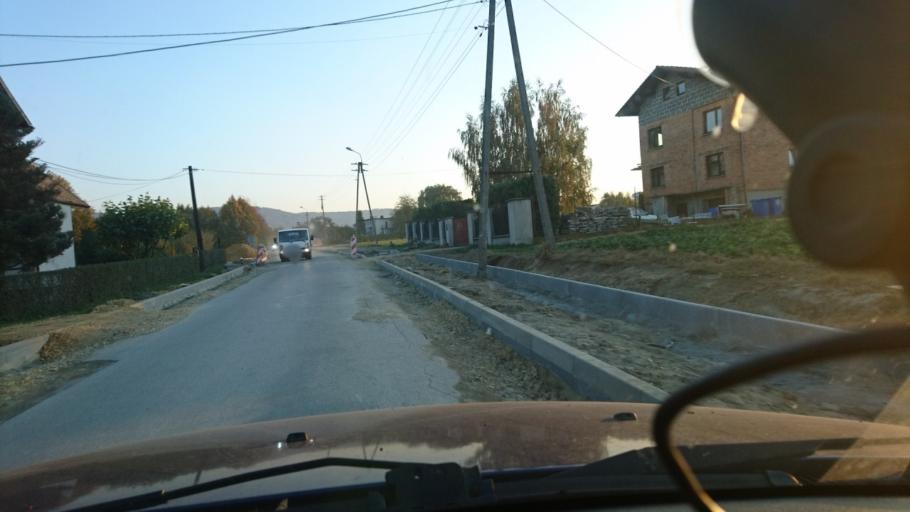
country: PL
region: Silesian Voivodeship
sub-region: Powiat bielski
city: Pisarzowice
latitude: 49.8664
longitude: 19.1379
